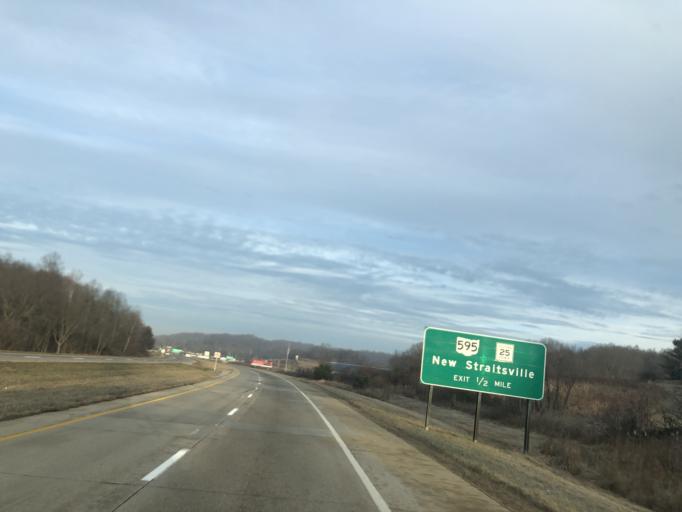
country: US
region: Ohio
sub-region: Athens County
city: Nelsonville
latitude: 39.4868
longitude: -82.3208
